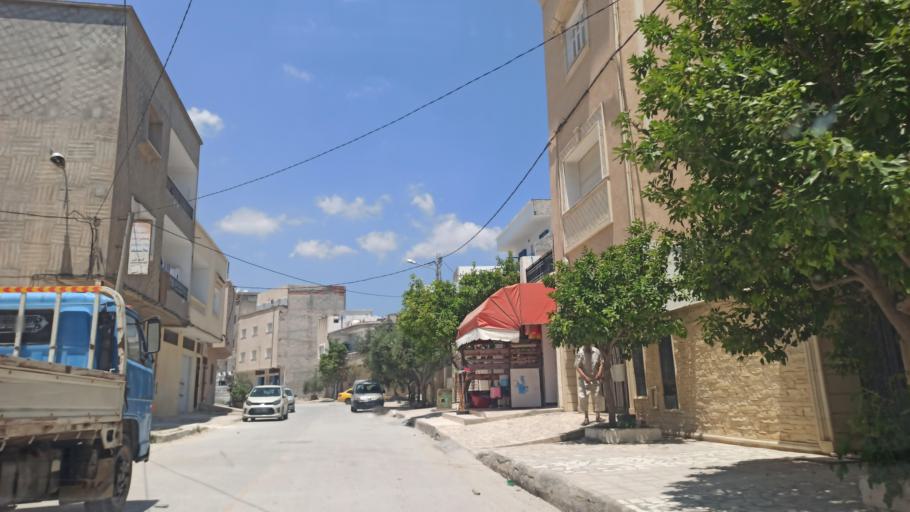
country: TN
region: Nabul
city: Dar Chabanne
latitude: 36.4681
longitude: 10.7435
